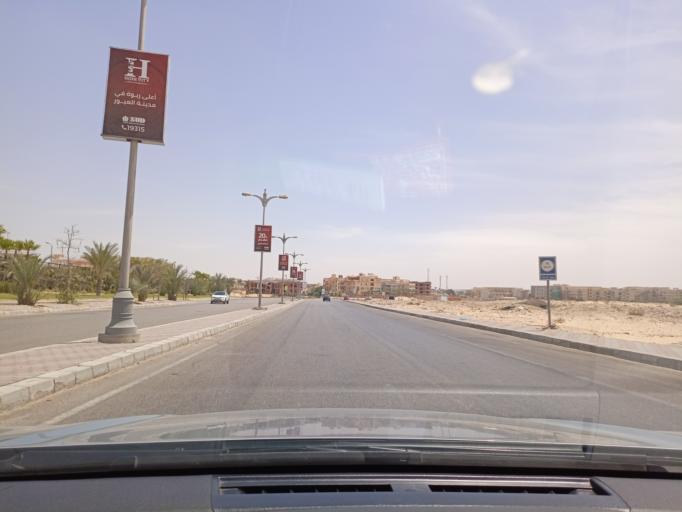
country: EG
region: Muhafazat al Qalyubiyah
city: Al Khankah
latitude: 30.1728
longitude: 31.4851
